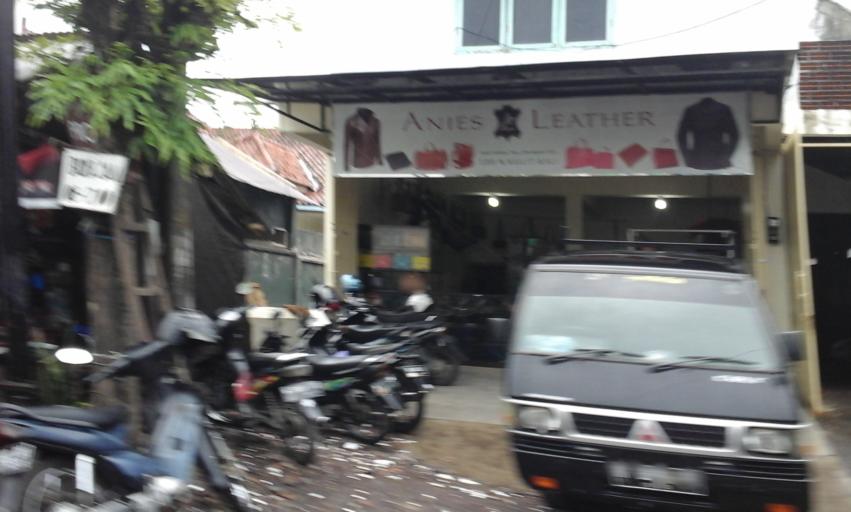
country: ID
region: East Java
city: Rogotrunan
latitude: -8.1250
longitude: 113.2261
